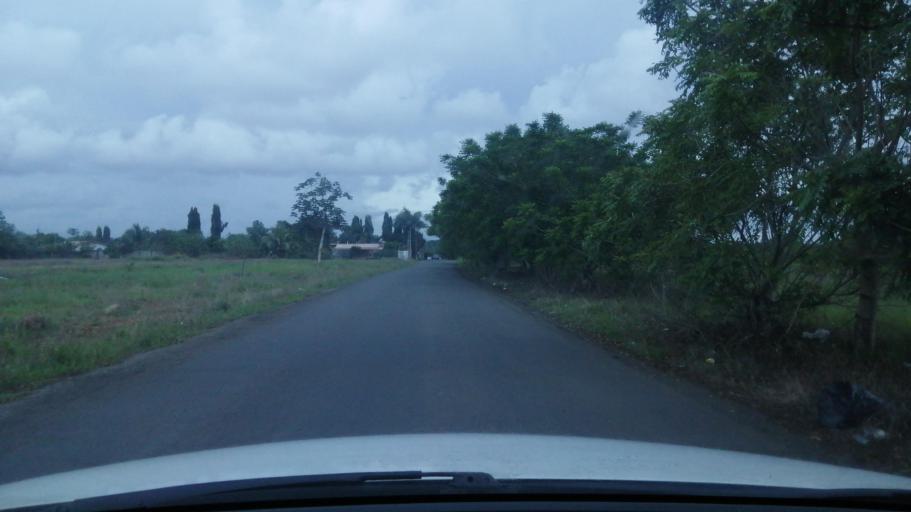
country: PA
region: Chiriqui
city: David
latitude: 8.4056
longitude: -82.4528
